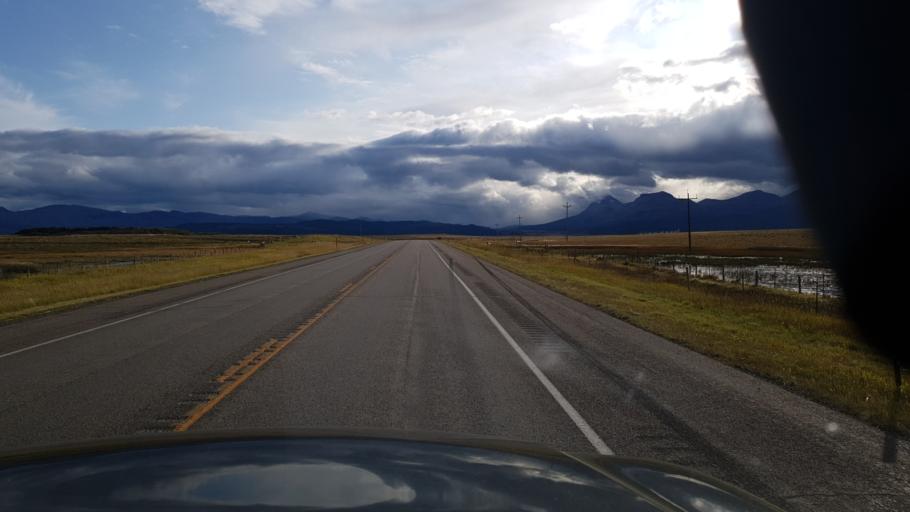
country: US
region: Montana
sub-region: Glacier County
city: South Browning
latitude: 48.4711
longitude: -113.1495
